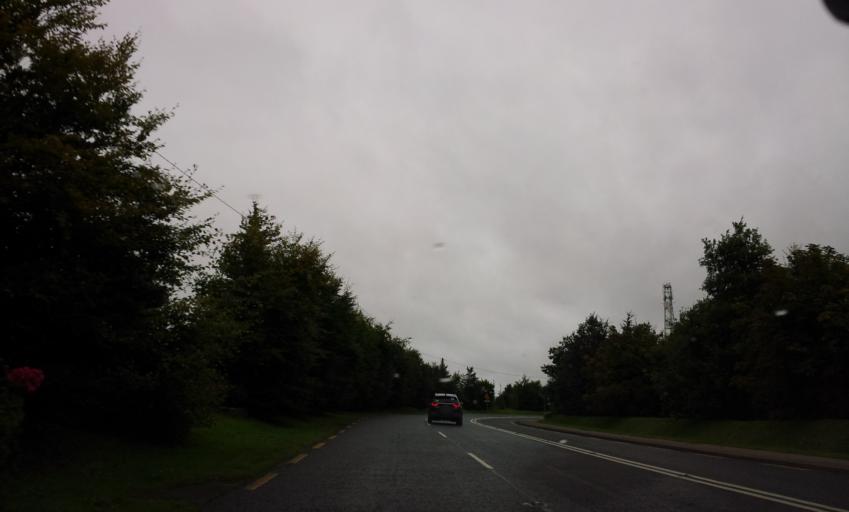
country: IE
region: Munster
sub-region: County Cork
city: Mitchelstown
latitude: 52.2466
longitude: -8.4190
